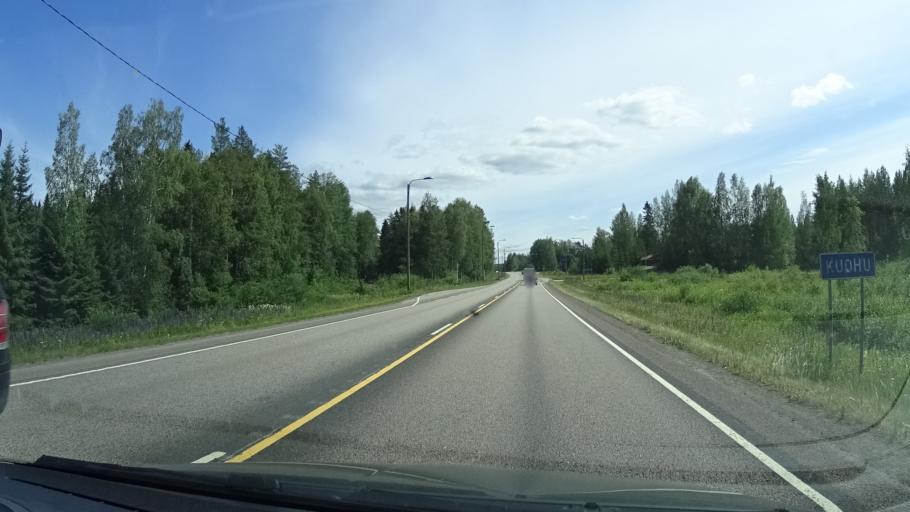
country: FI
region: Central Finland
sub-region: Jyvaeskylae
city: Uurainen
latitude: 62.2664
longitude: 25.4431
